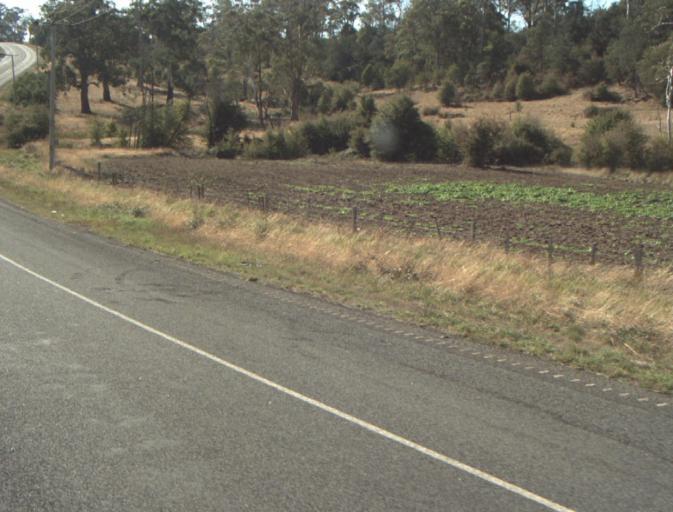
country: AU
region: Tasmania
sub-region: Launceston
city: Mayfield
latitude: -41.3495
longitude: 147.0969
